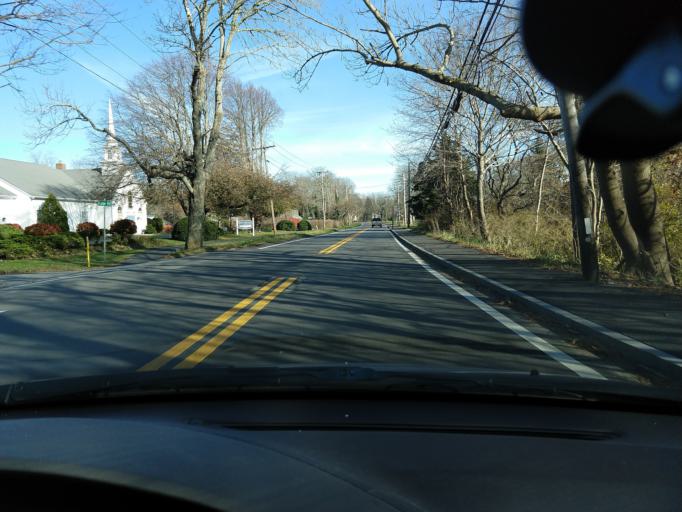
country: US
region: Massachusetts
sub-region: Barnstable County
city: Brewster
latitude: 41.7657
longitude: -70.0648
